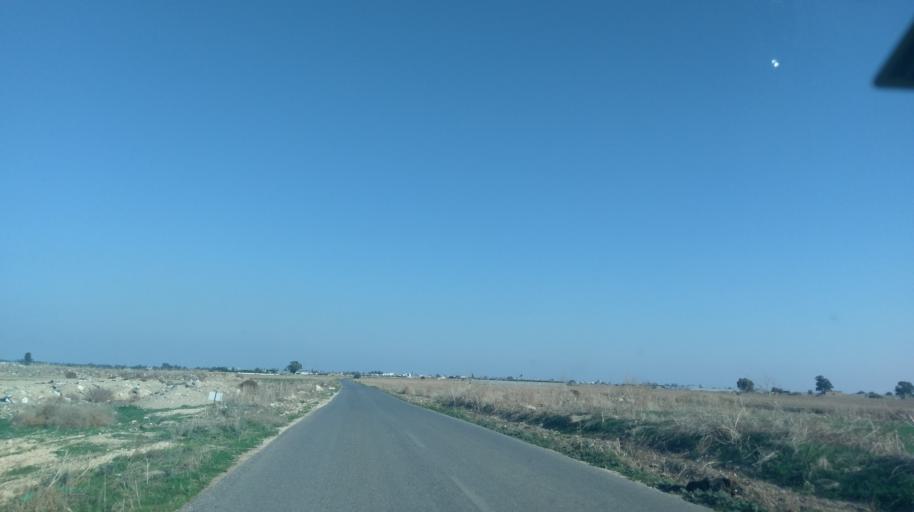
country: CY
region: Larnaka
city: Pergamos
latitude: 35.1018
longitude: 33.6591
